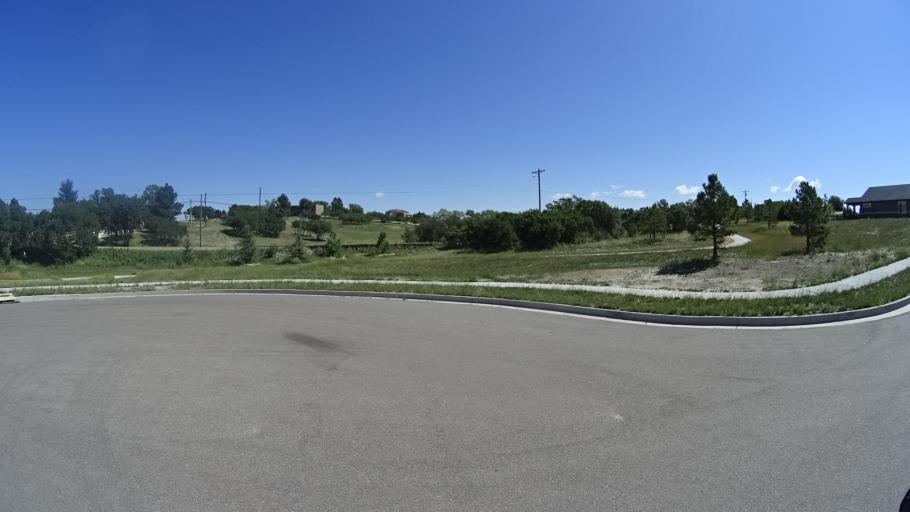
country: US
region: Colorado
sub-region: El Paso County
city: Black Forest
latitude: 38.9832
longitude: -104.7527
